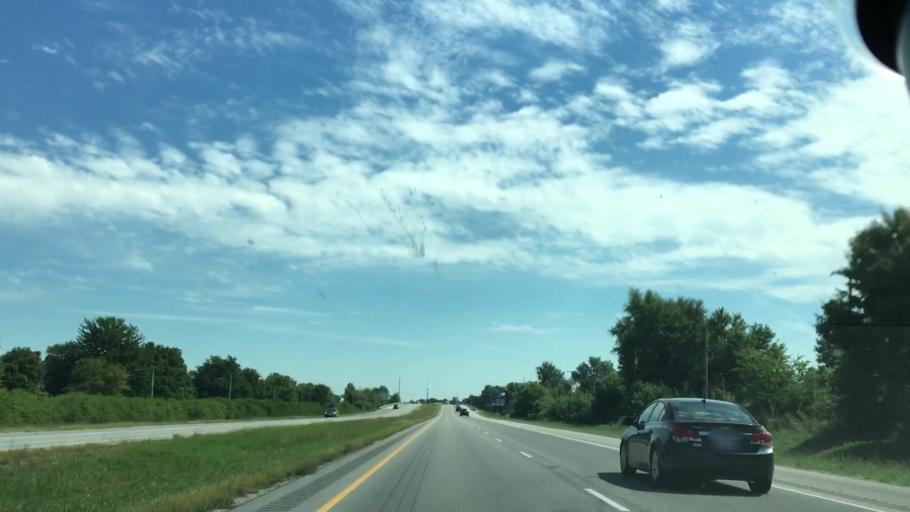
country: US
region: Kentucky
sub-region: Daviess County
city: Owensboro
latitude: 37.7370
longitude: -87.1410
